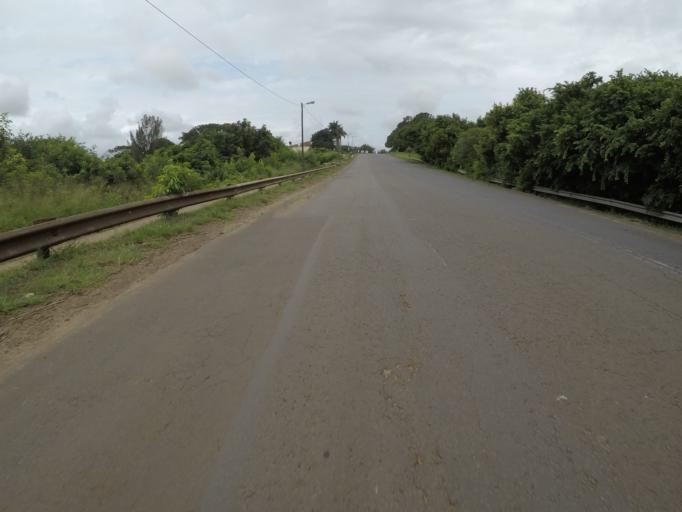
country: ZA
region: KwaZulu-Natal
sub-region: uThungulu District Municipality
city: Empangeni
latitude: -28.7757
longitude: 31.8891
